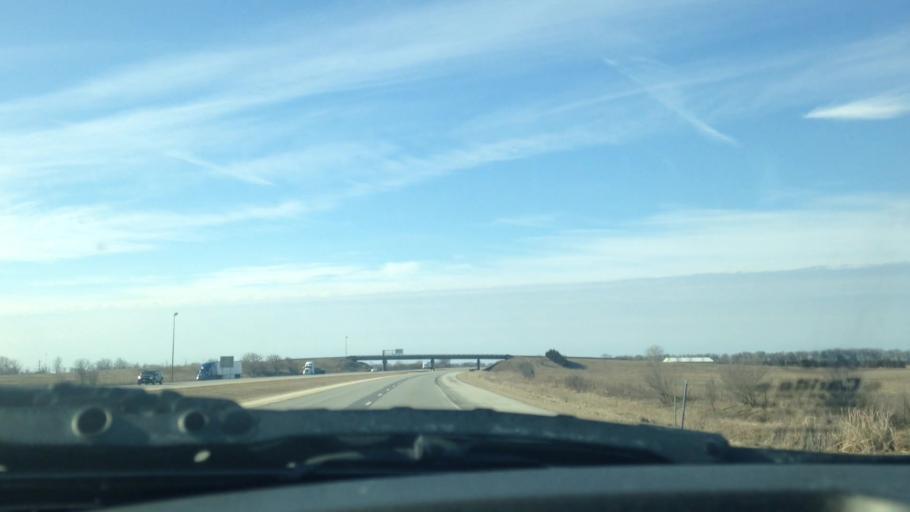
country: US
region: Illinois
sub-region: Ford County
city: Paxton
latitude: 40.5503
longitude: -88.0621
